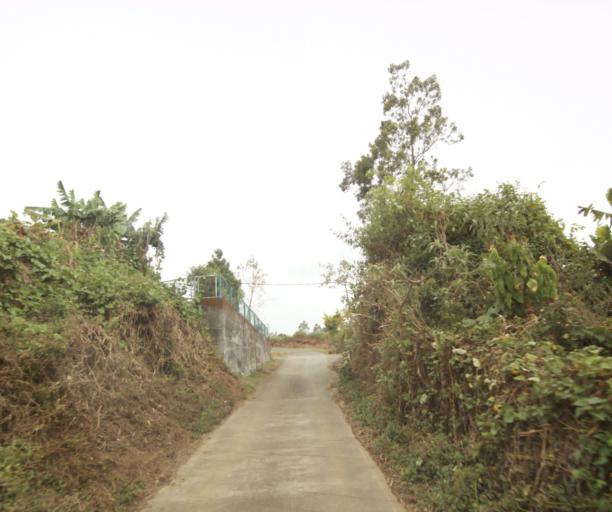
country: RE
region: Reunion
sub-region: Reunion
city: Saint-Paul
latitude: -21.0113
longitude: 55.3482
